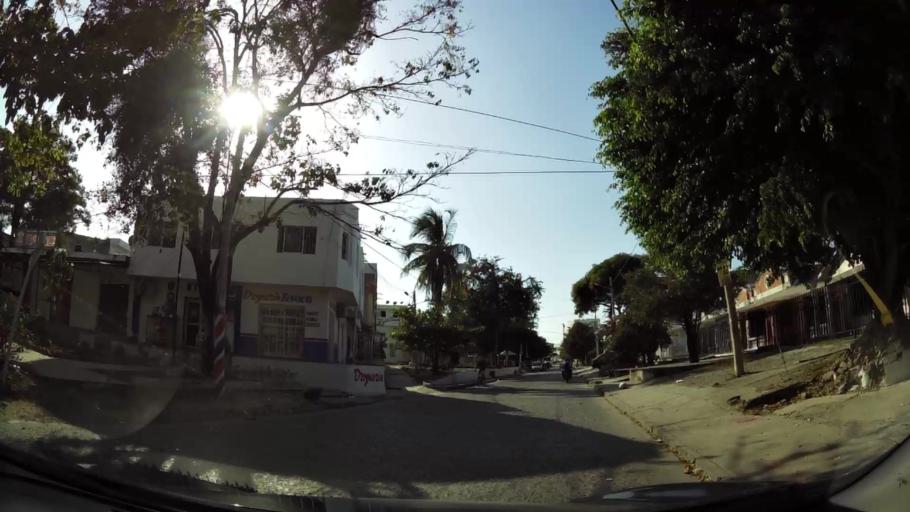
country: CO
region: Bolivar
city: Cartagena
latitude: 10.3833
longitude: -75.4833
